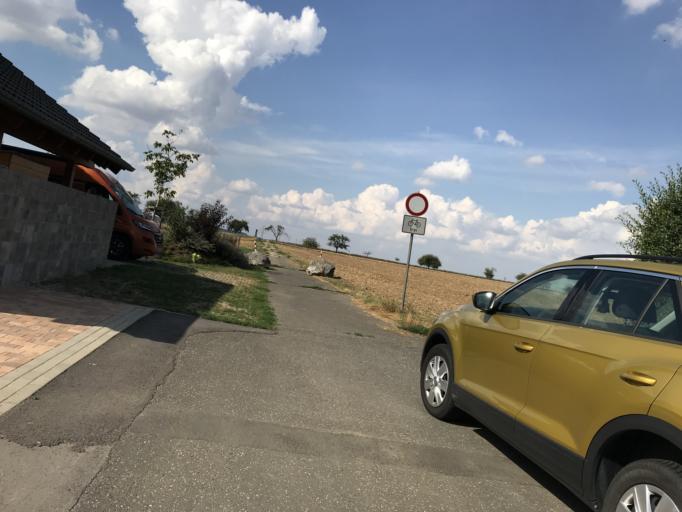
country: DE
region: Hesse
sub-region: Regierungsbezirk Darmstadt
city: Wolfersheim
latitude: 50.3640
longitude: 8.8171
